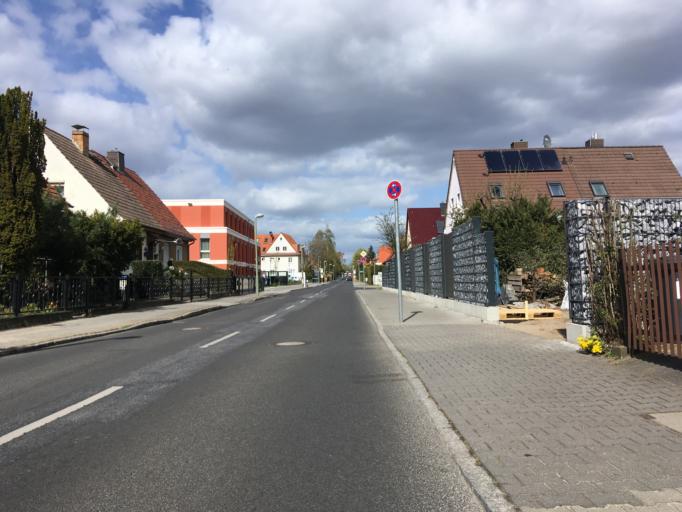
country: DE
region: Berlin
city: Altglienicke
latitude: 52.4115
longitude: 13.5359
